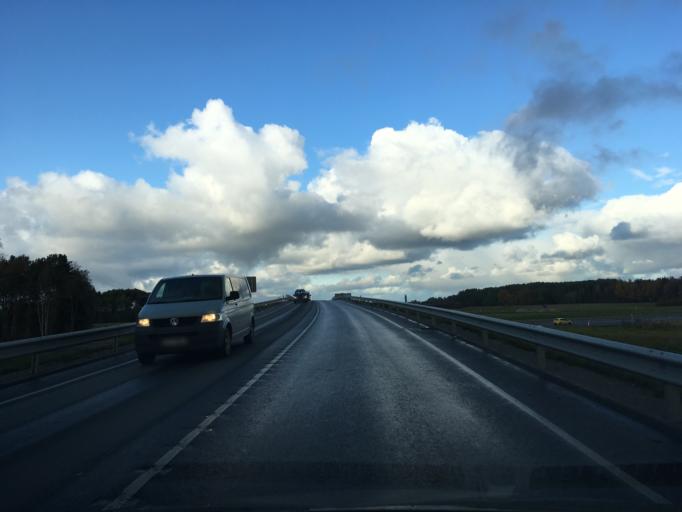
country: EE
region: Harju
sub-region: Saku vald
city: Saku
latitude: 59.3145
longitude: 24.6413
